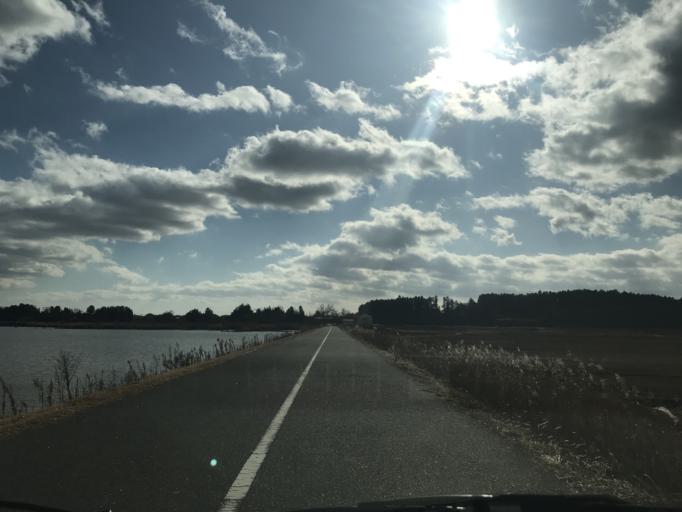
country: JP
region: Miyagi
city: Kogota
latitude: 38.7252
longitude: 141.0752
